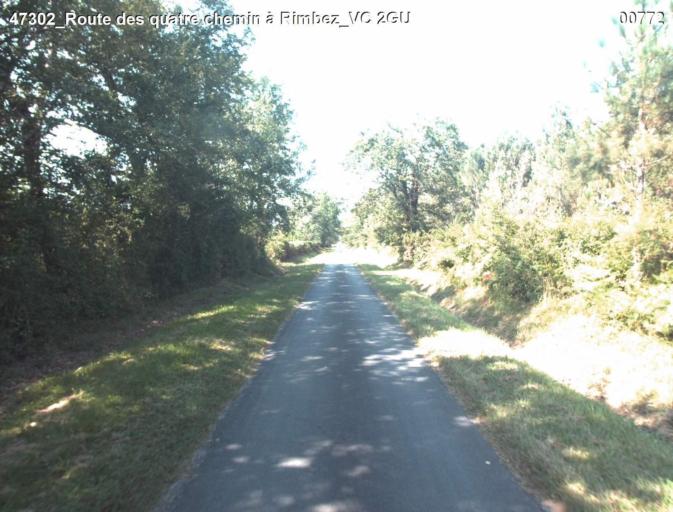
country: FR
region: Aquitaine
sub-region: Departement des Landes
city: Gabarret
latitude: 44.0285
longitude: 0.0826
